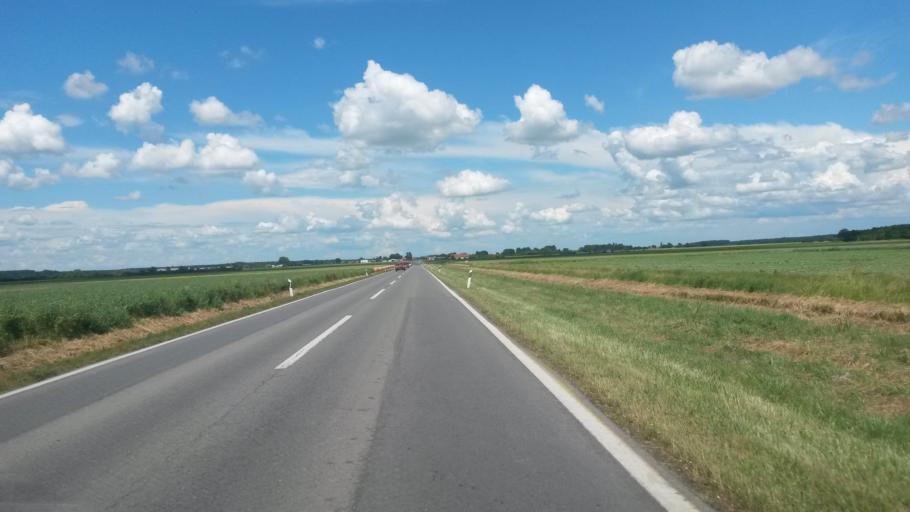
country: HR
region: Osjecko-Baranjska
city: Viskovci
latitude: 45.3848
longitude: 18.4477
